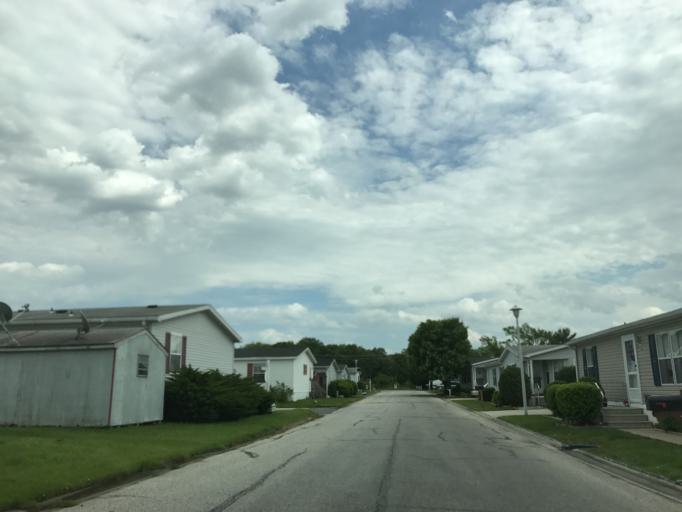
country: US
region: Maryland
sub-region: Baltimore County
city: Bowleys Quarters
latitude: 39.3380
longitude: -76.4095
